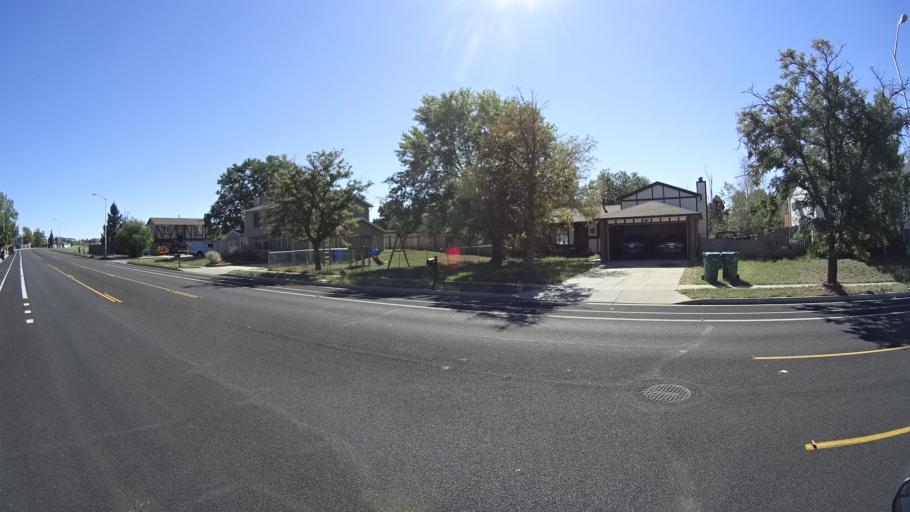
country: US
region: Colorado
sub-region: El Paso County
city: Cimarron Hills
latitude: 38.8163
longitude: -104.7343
